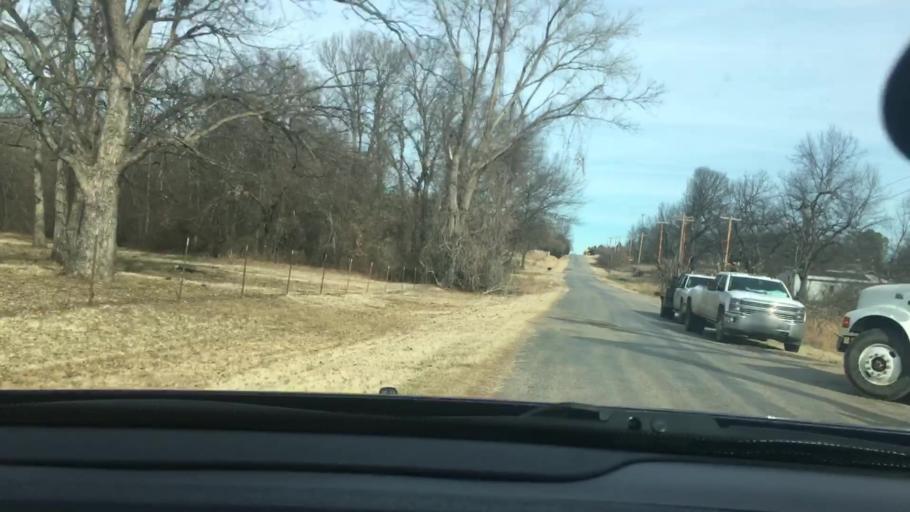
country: US
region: Oklahoma
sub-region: Garvin County
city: Wynnewood
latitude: 34.6458
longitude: -97.2476
